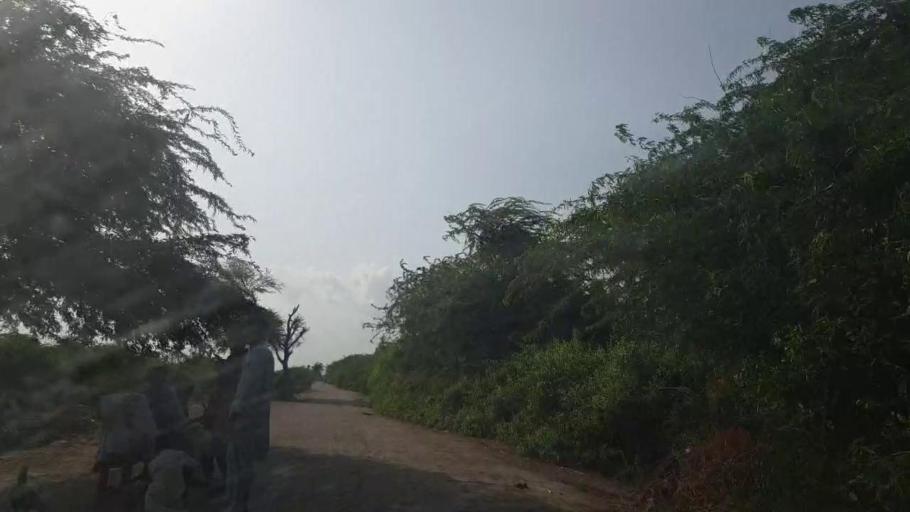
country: PK
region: Sindh
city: Tando Bago
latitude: 24.7572
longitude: 69.0841
